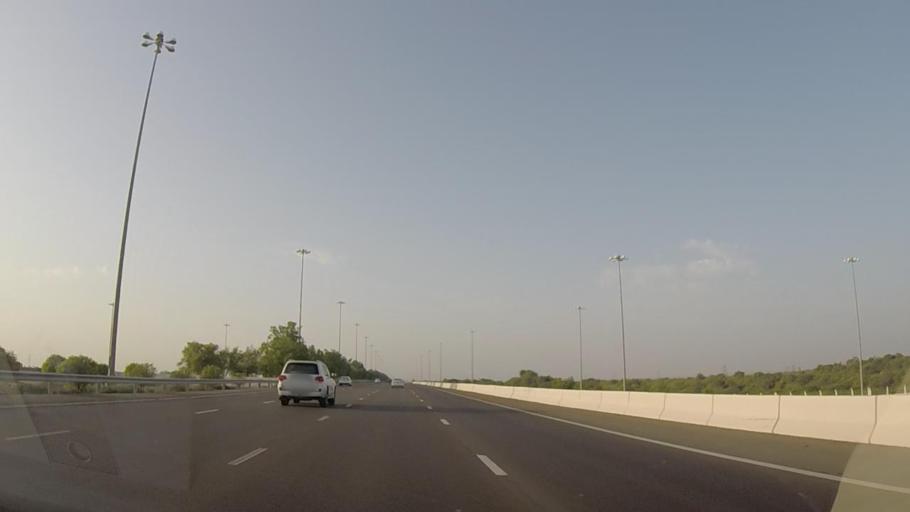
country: AE
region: Dubai
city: Dubai
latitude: 24.7987
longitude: 54.8631
